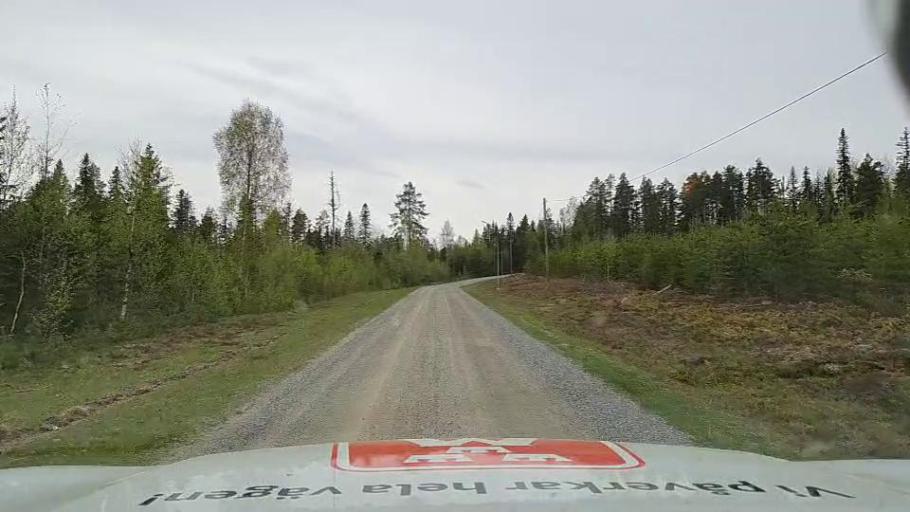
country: SE
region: Jaemtland
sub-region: Bergs Kommun
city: Hoverberg
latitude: 62.5652
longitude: 14.6743
